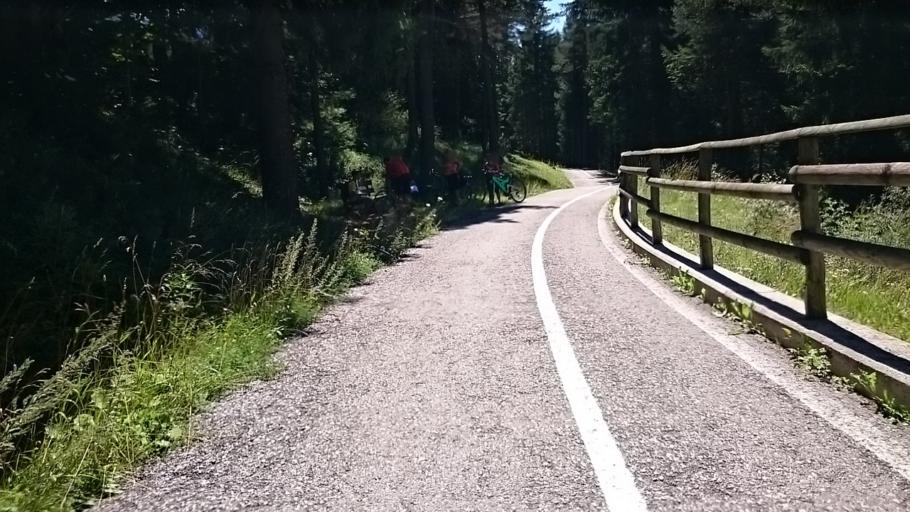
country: IT
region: Veneto
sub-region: Provincia di Belluno
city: San Vito
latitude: 46.4864
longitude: 12.1907
